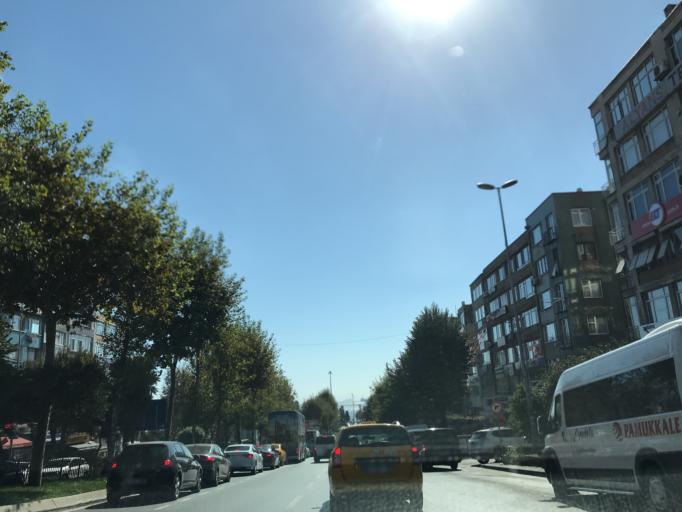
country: TR
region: Istanbul
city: Sisli
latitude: 41.0452
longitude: 29.0073
